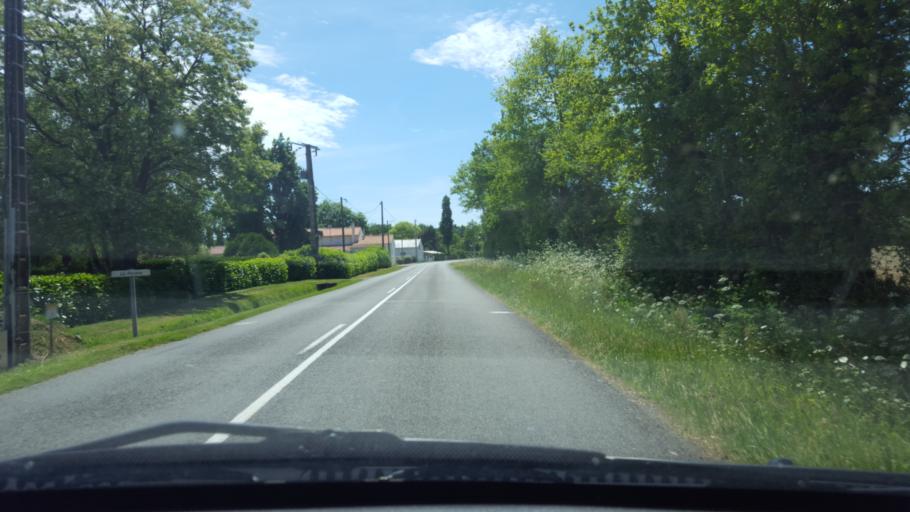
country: FR
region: Pays de la Loire
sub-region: Departement de la Loire-Atlantique
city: Touvois
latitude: 46.9129
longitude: -1.6830
